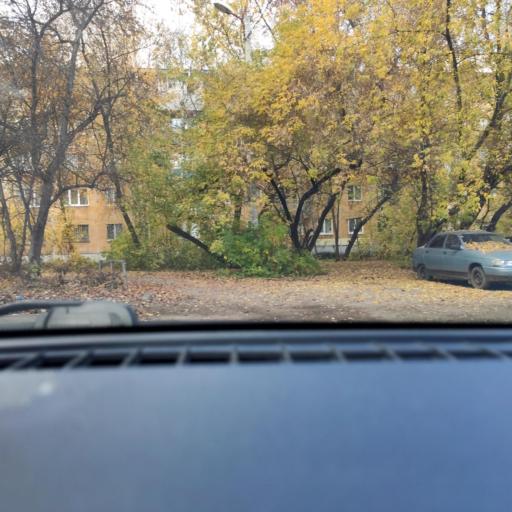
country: RU
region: Perm
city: Perm
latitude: 57.9962
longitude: 56.2974
